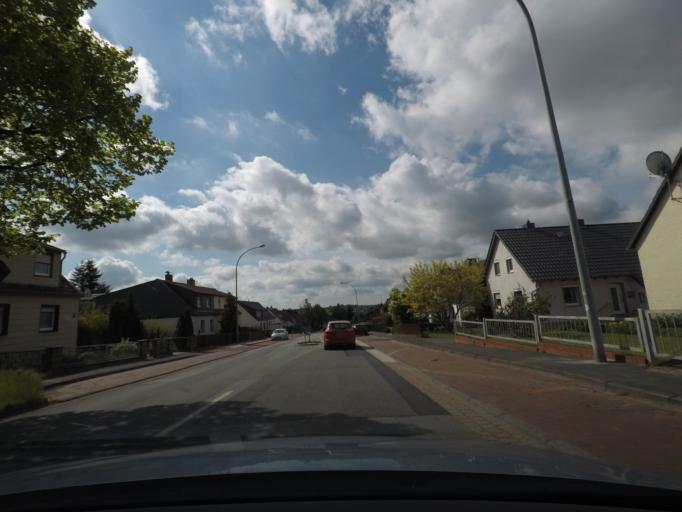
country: DE
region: Lower Saxony
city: Helmstedt
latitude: 52.2436
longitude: 10.9982
